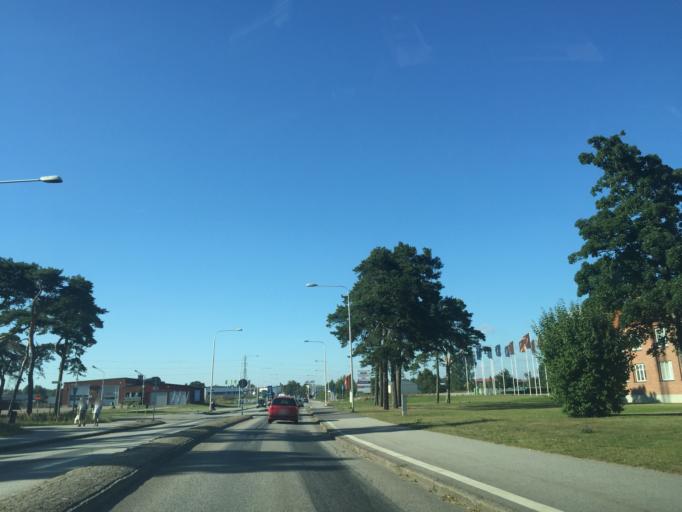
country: SE
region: Skane
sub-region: Ystads Kommun
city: Ystad
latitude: 55.4329
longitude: 13.8390
